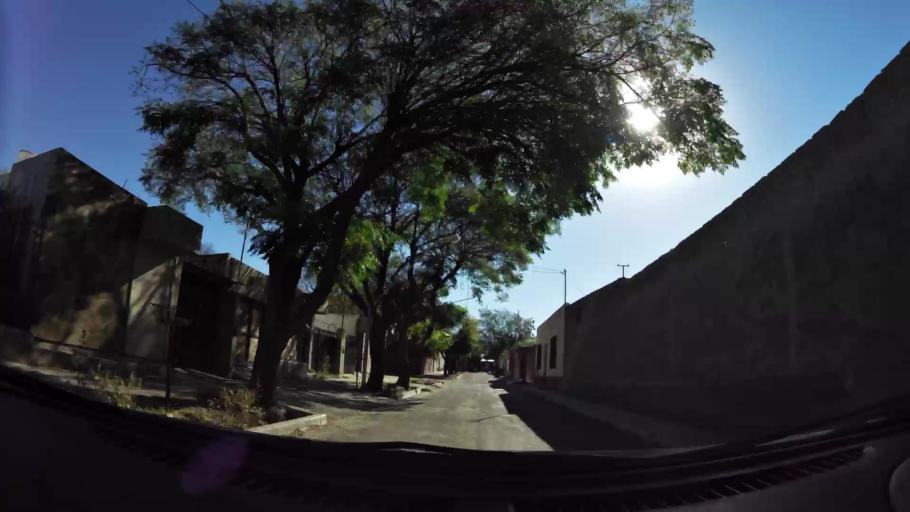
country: AR
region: Mendoza
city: Las Heras
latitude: -32.8546
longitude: -68.8304
